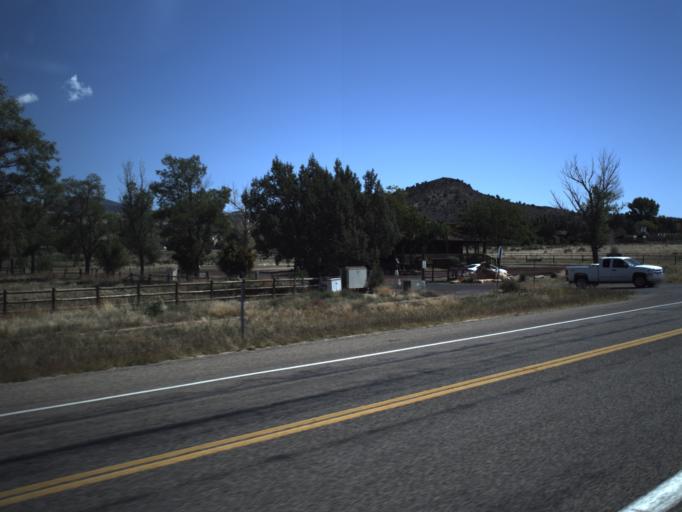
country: US
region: Utah
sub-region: Washington County
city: Ivins
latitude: 37.3057
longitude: -113.6708
